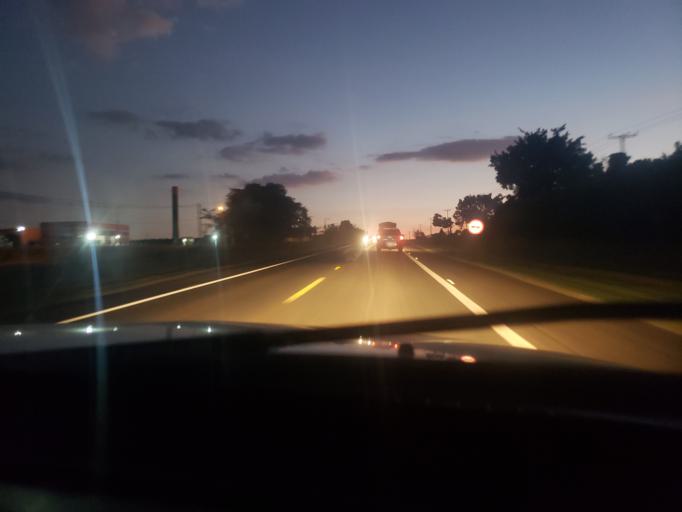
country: BR
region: Sao Paulo
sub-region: Conchal
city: Conchal
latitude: -22.3253
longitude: -47.1454
